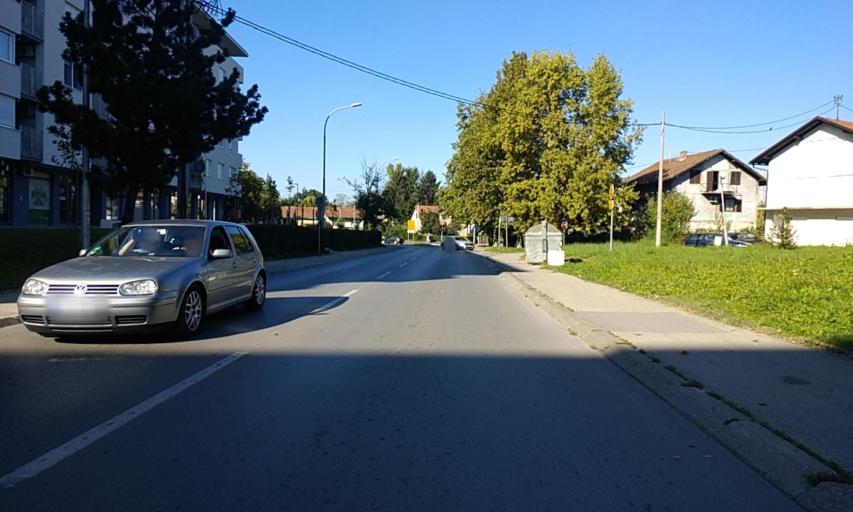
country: BA
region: Republika Srpska
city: Starcevica
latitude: 44.7652
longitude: 17.2121
